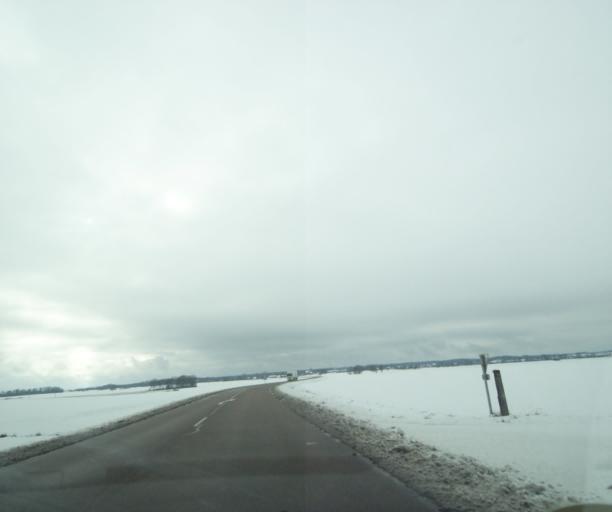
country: FR
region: Champagne-Ardenne
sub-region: Departement de la Haute-Marne
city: Montier-en-Der
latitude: 48.4455
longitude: 4.7334
